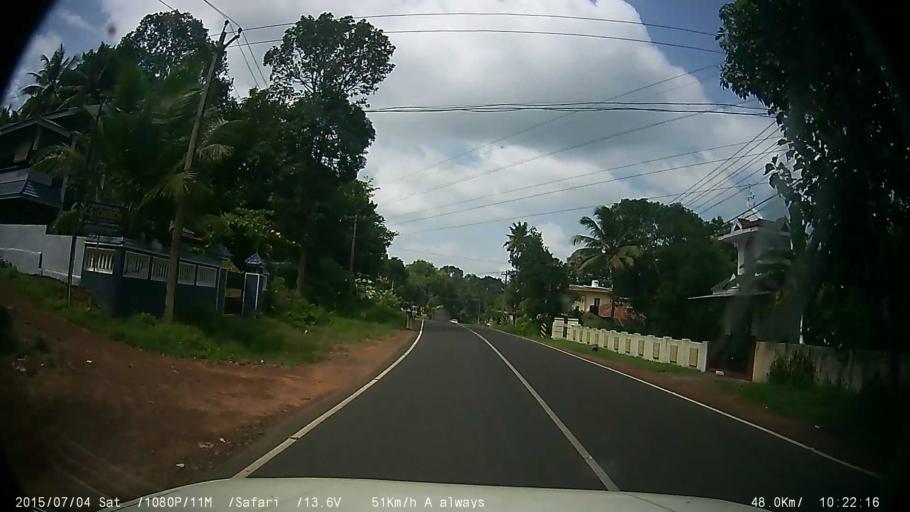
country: IN
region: Kerala
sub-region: Kottayam
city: Changanacheri
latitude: 9.4346
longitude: 76.5667
